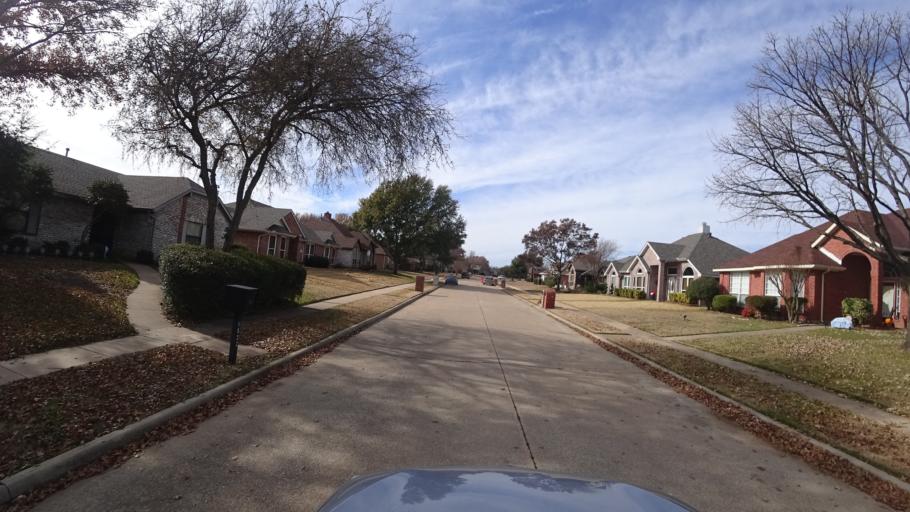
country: US
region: Texas
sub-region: Denton County
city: Highland Village
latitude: 33.0629
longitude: -97.0370
